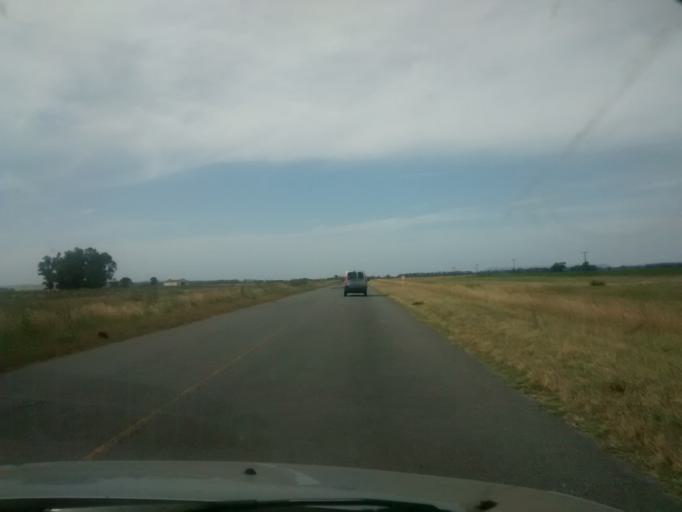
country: AR
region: Buenos Aires
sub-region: Partido de Loberia
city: Loberia
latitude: -38.0309
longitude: -58.7331
